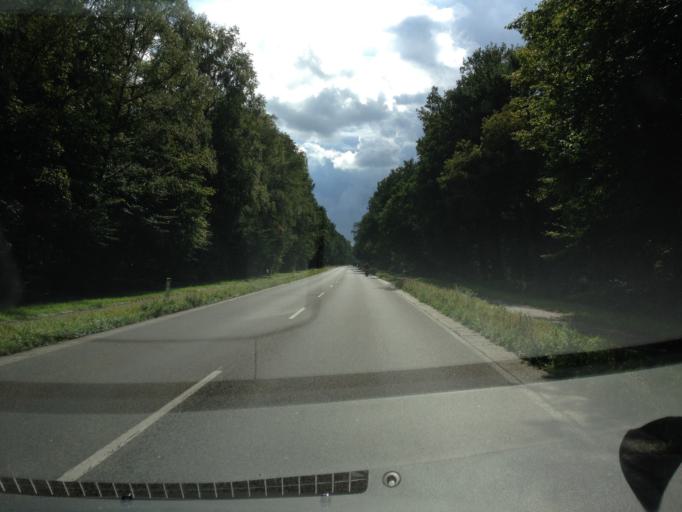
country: DE
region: North Rhine-Westphalia
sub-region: Regierungsbezirk Koln
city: Eil
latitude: 50.8916
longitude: 7.1017
